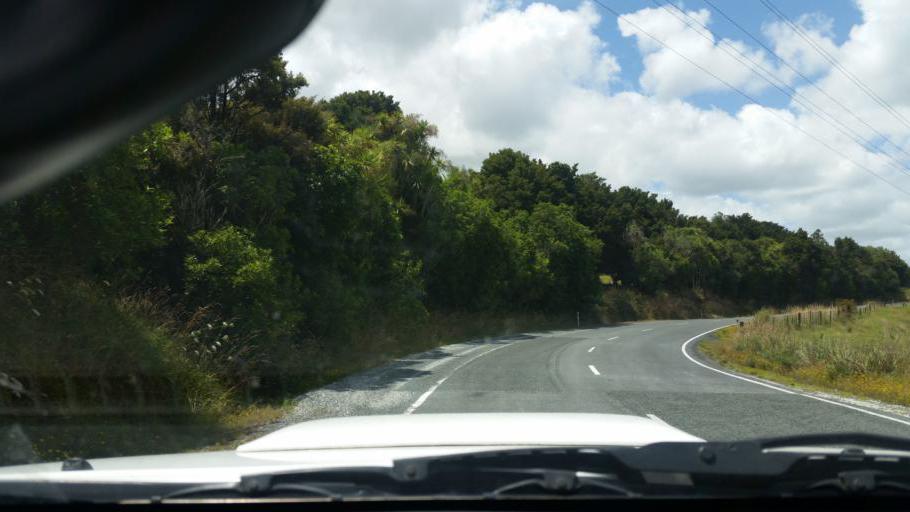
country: NZ
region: Northland
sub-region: Whangarei
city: Ruakaka
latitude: -36.0738
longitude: 174.2605
